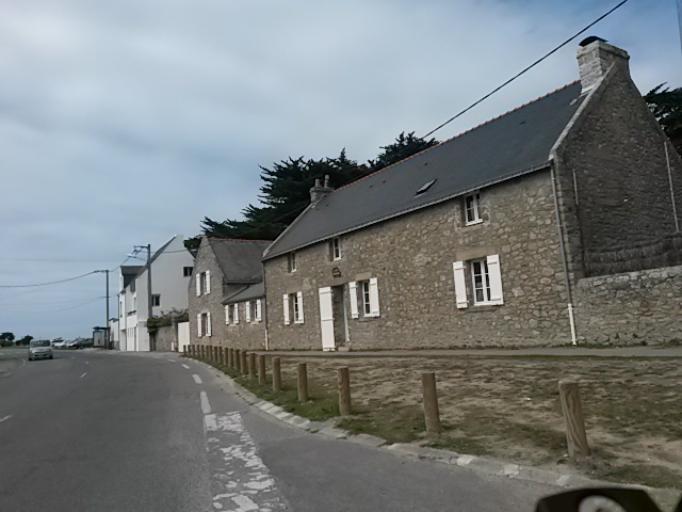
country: FR
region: Pays de la Loire
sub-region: Departement de la Loire-Atlantique
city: Le Croisic
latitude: 47.3009
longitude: -2.5267
